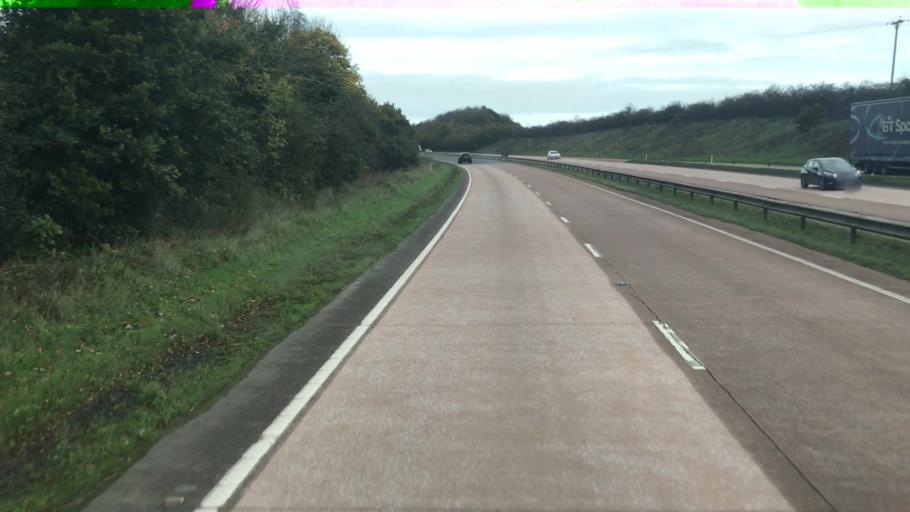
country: GB
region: England
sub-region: Devon
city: Okehampton
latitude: 50.7266
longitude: -3.8563
